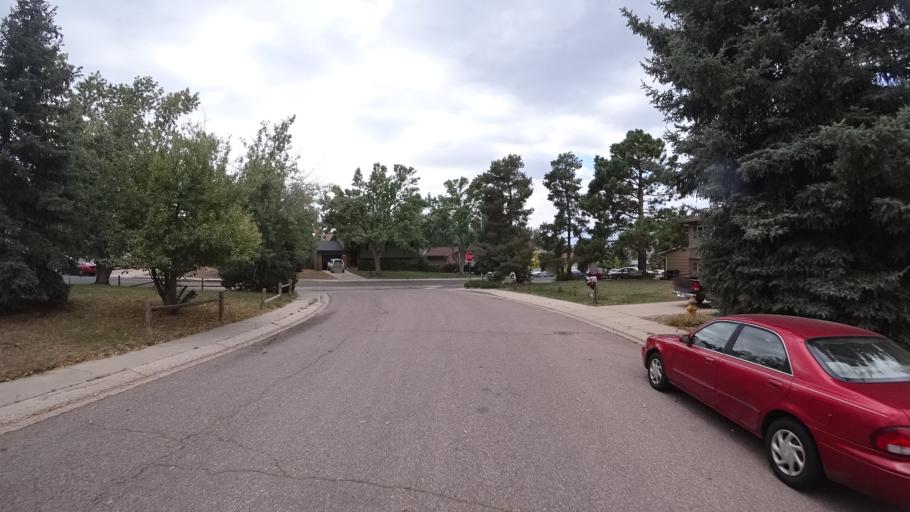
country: US
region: Colorado
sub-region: El Paso County
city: Cimarron Hills
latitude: 38.8894
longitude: -104.7353
